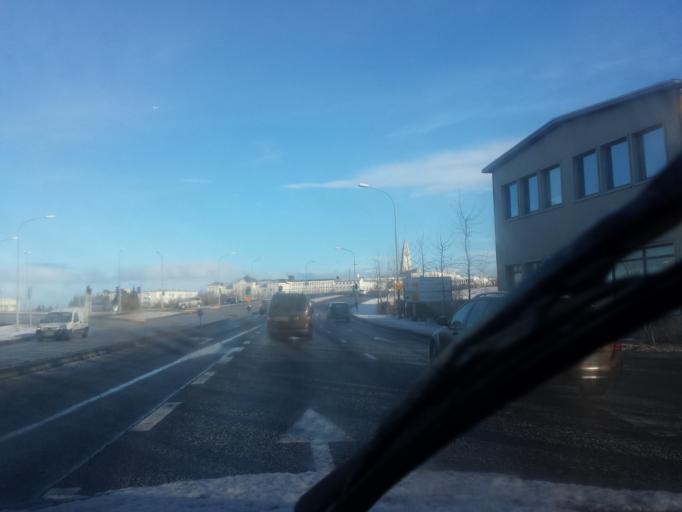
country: IS
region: Capital Region
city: Kopavogur
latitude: 64.1345
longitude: -21.9226
